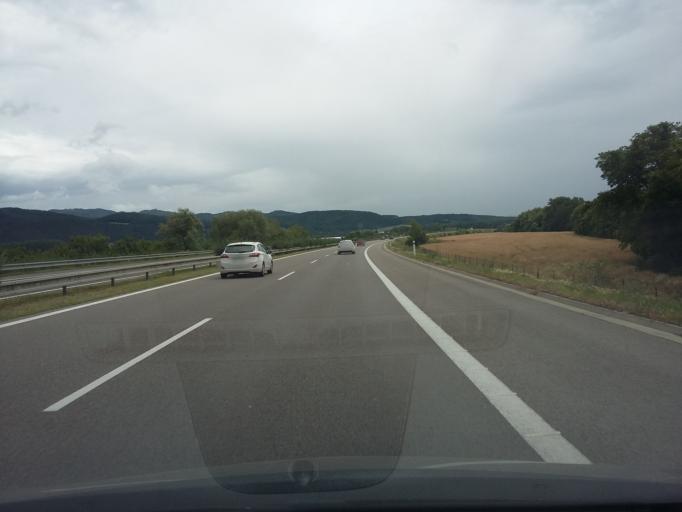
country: SK
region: Trenciansky
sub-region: Okres Nove Mesto nad Vahom
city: Nove Mesto nad Vahom
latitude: 48.7271
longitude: 17.8727
